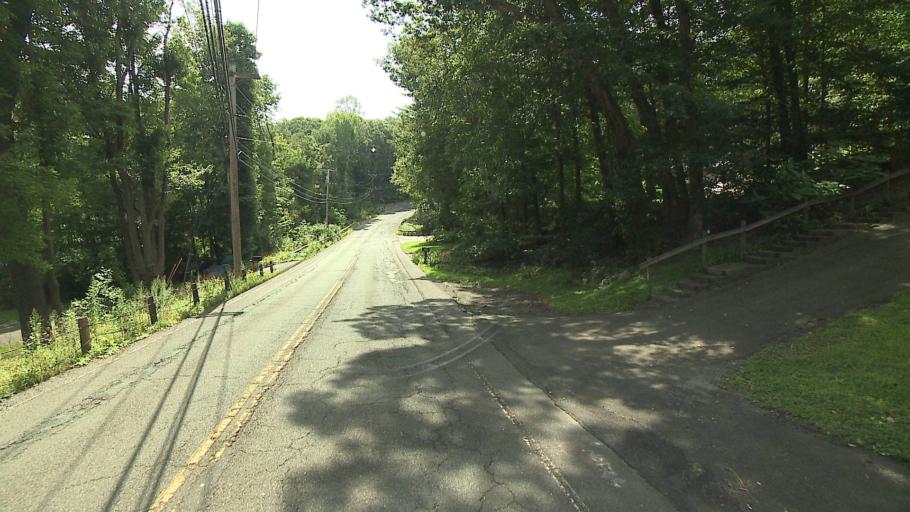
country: US
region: New York
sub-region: Putnam County
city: Putnam Lake
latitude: 41.4702
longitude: -73.5008
